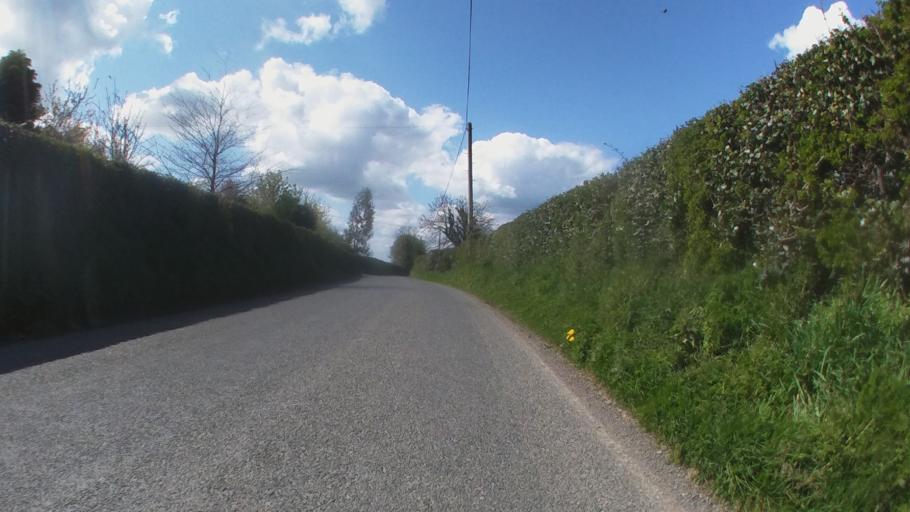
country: IE
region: Leinster
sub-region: Kilkenny
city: Kilkenny
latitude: 52.6613
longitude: -7.1993
